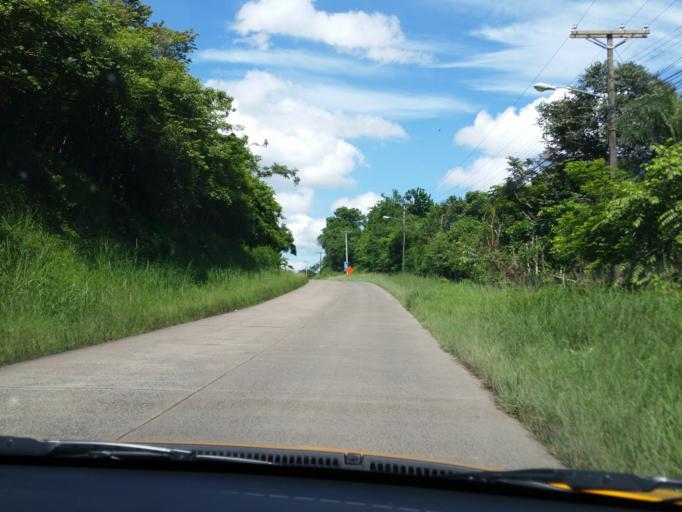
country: PA
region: Panama
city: San Miguelito
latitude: 9.0723
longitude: -79.4673
